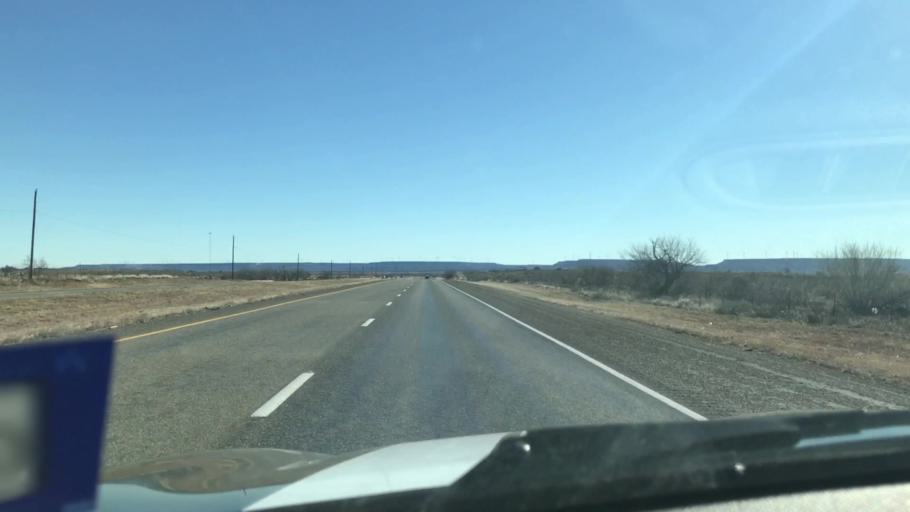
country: US
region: Texas
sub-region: Garza County
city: Post
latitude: 33.0843
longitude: -101.2418
